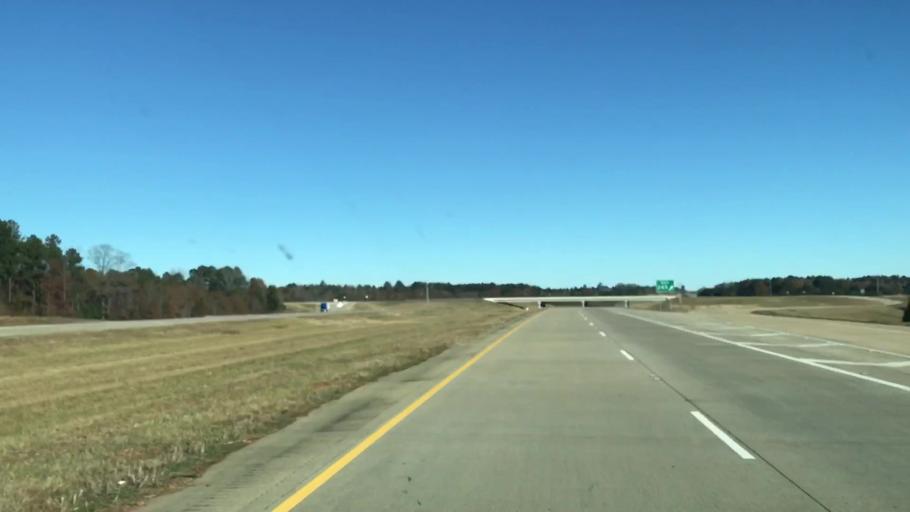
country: US
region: Louisiana
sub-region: Caddo Parish
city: Vivian
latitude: 32.9923
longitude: -93.9105
